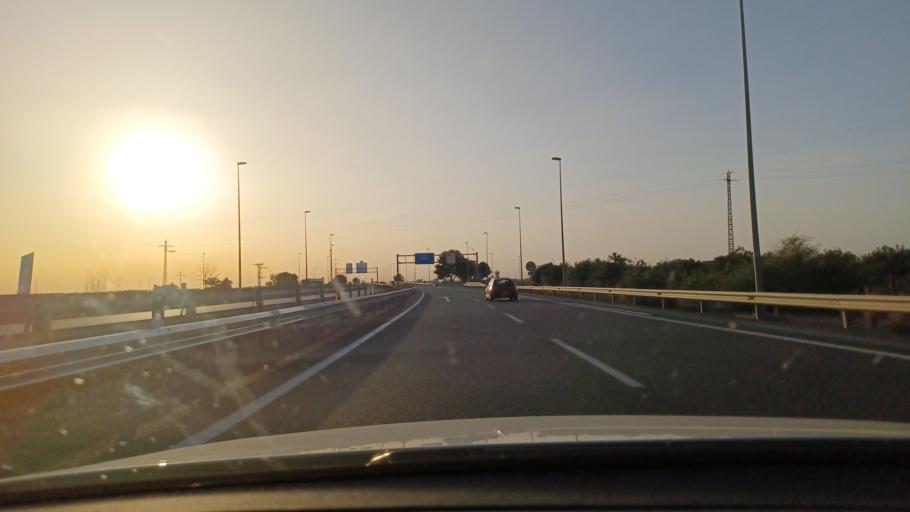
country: ES
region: Valencia
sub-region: Provincia de Valencia
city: Pucol
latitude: 39.6314
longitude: -0.3028
